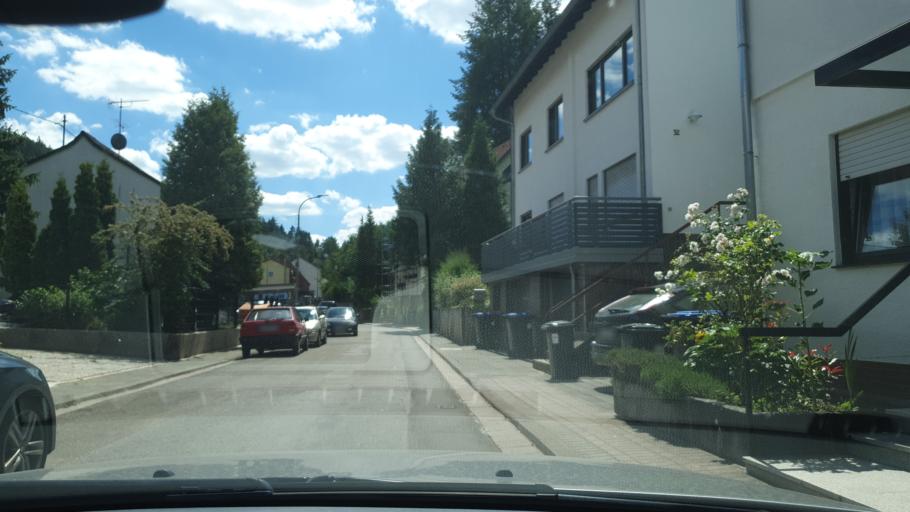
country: DE
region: Rheinland-Pfalz
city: Trippstadt
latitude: 49.3772
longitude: 7.8217
